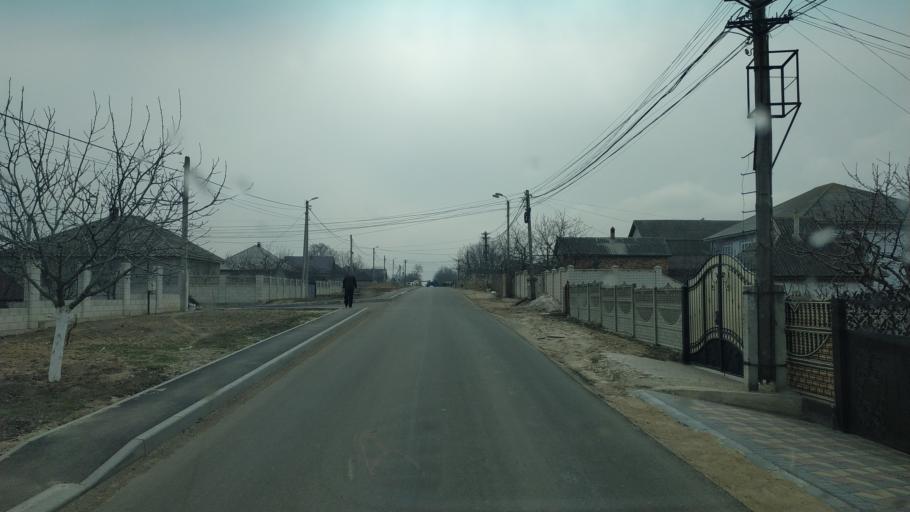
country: MD
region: Chisinau
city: Singera
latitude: 46.9060
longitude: 28.9869
